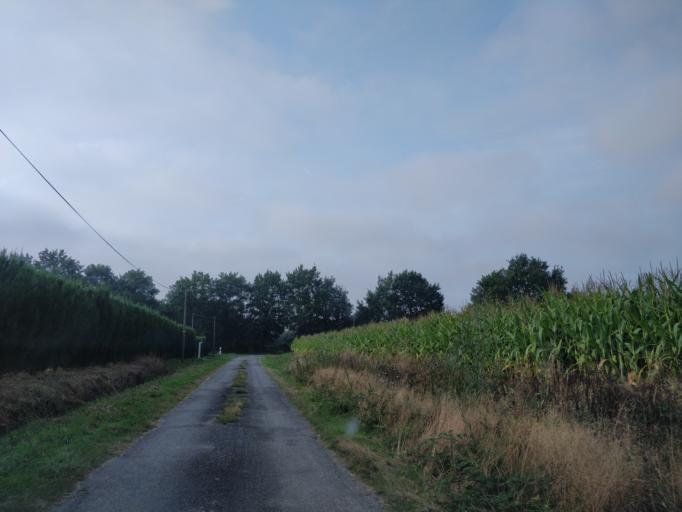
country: FR
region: Brittany
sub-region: Departement d'Ille-et-Vilaine
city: Noyal-sur-Vilaine
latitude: 48.1028
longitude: -1.5511
